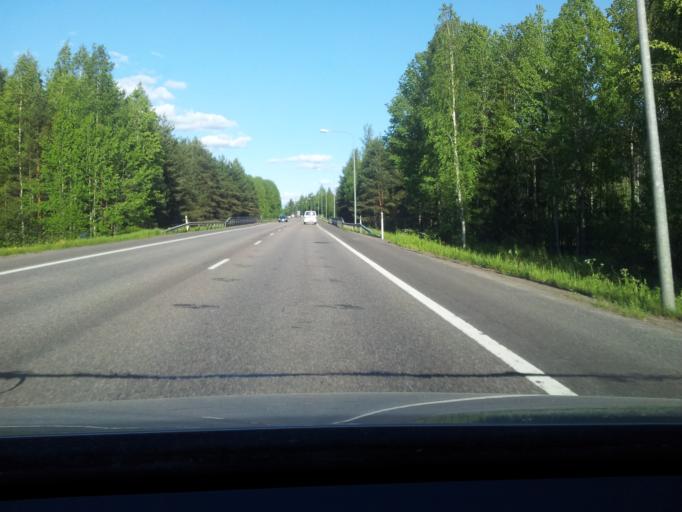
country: FI
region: Kymenlaakso
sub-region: Kouvola
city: Kouvola
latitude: 60.8731
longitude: 26.6266
